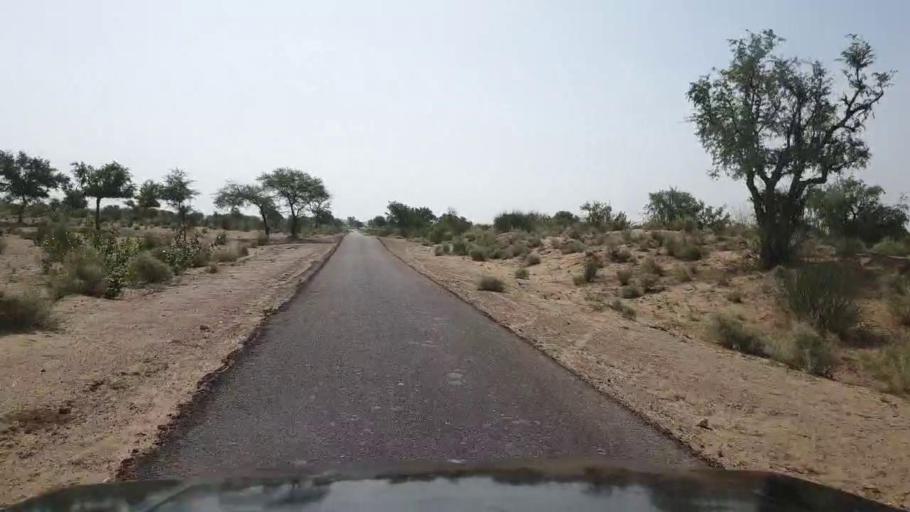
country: PK
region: Sindh
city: Islamkot
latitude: 24.9376
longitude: 70.0901
